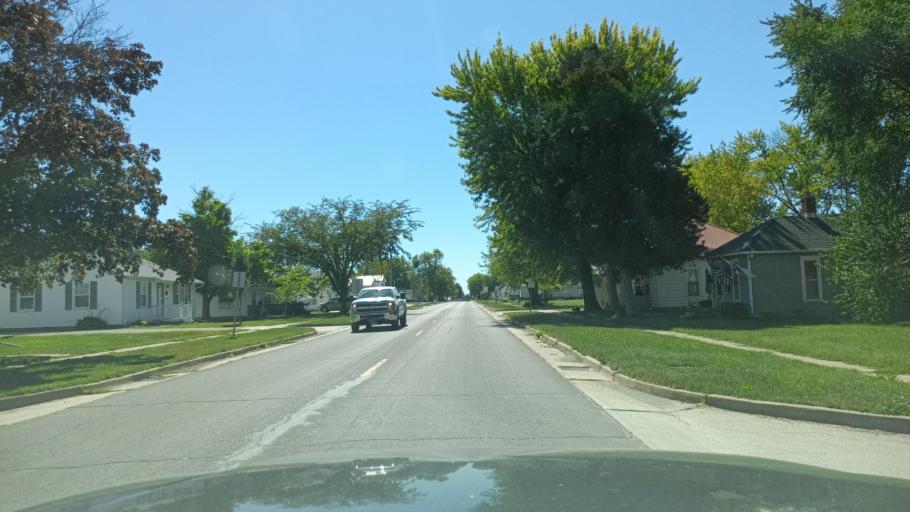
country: US
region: Missouri
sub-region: Macon County
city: La Plata
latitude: 40.0274
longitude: -92.4885
